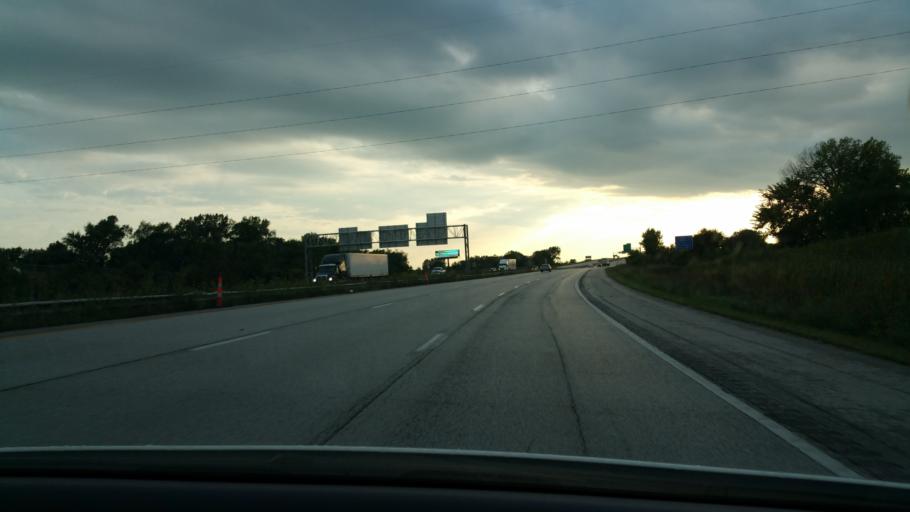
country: US
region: Iowa
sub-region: Polk County
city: Saylorville
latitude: 41.6515
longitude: -93.5813
